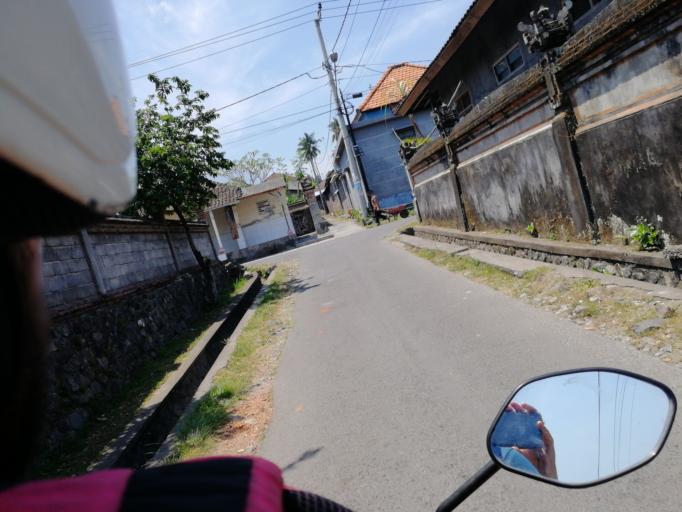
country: ID
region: Bali
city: Subagan
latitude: -8.4575
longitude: 115.5964
